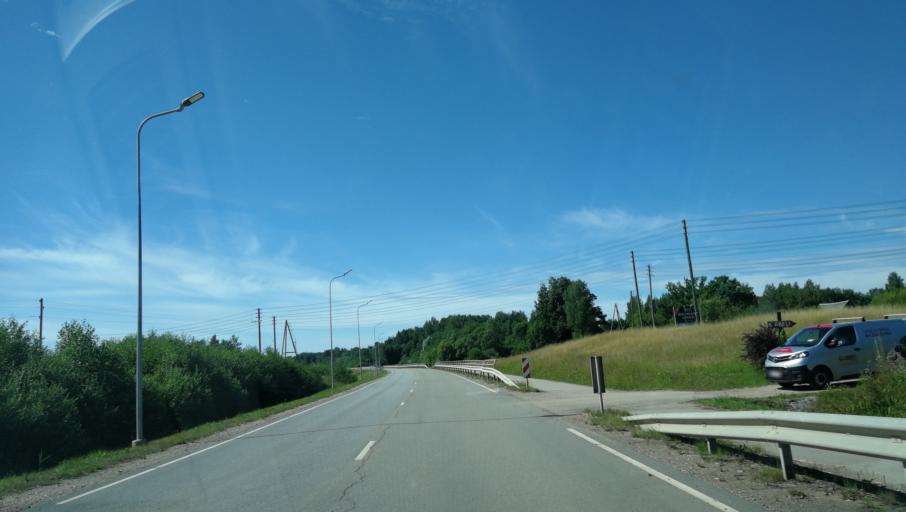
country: LV
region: Gulbenes Rajons
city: Gulbene
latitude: 57.1702
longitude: 26.7381
